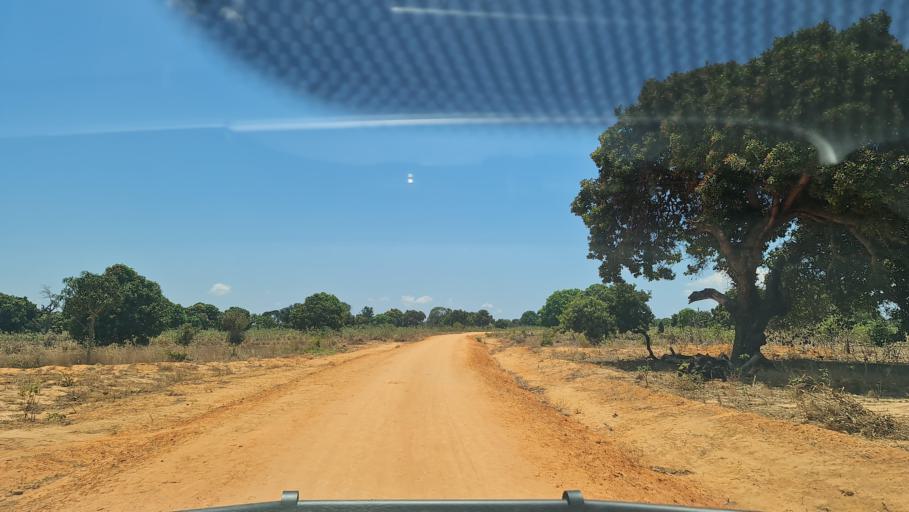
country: MZ
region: Nampula
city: Nacala
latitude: -14.2226
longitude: 40.6850
